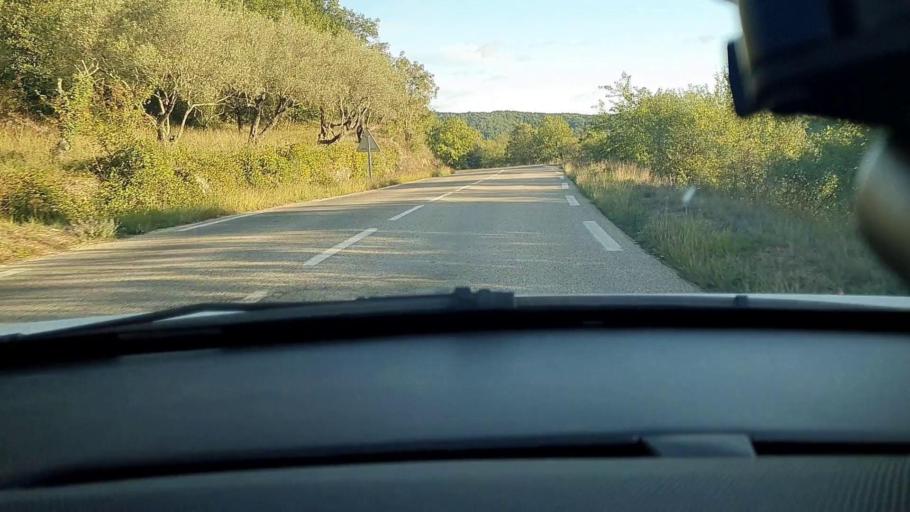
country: FR
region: Languedoc-Roussillon
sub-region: Departement du Gard
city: Barjac
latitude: 44.2363
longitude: 4.3041
